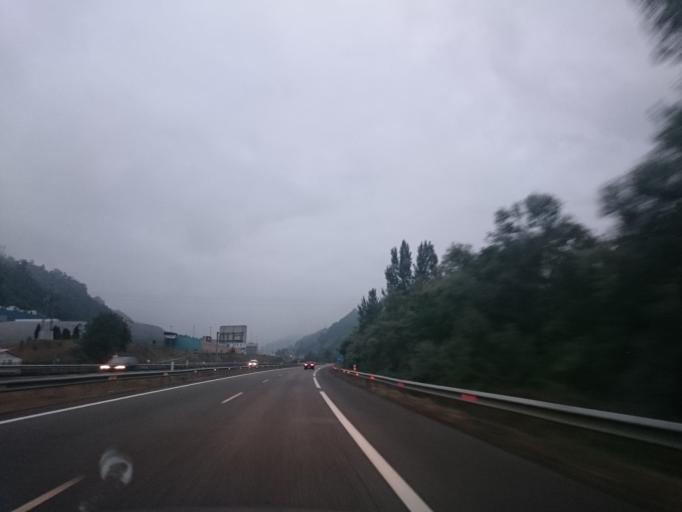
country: ES
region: Asturias
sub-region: Province of Asturias
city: Mieres
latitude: 43.2320
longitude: -5.7811
